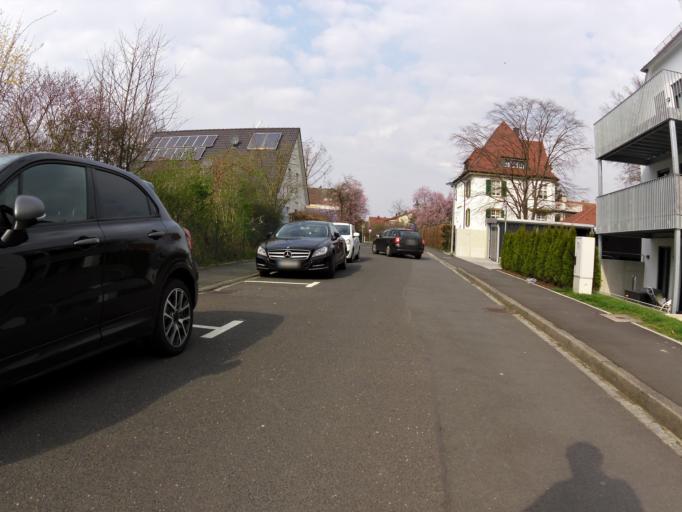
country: DE
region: Bavaria
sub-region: Regierungsbezirk Unterfranken
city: Kitzingen
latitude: 49.7291
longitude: 10.1630
